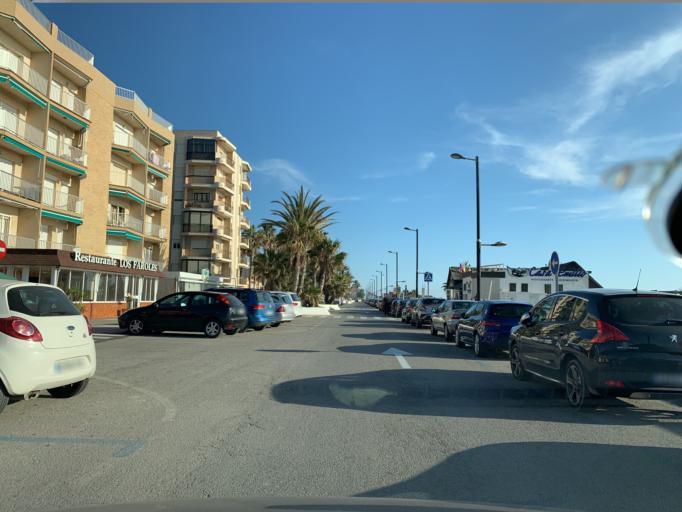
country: ES
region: Andalusia
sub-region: Provincia de Granada
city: Salobrena
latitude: 36.7329
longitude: -3.5883
